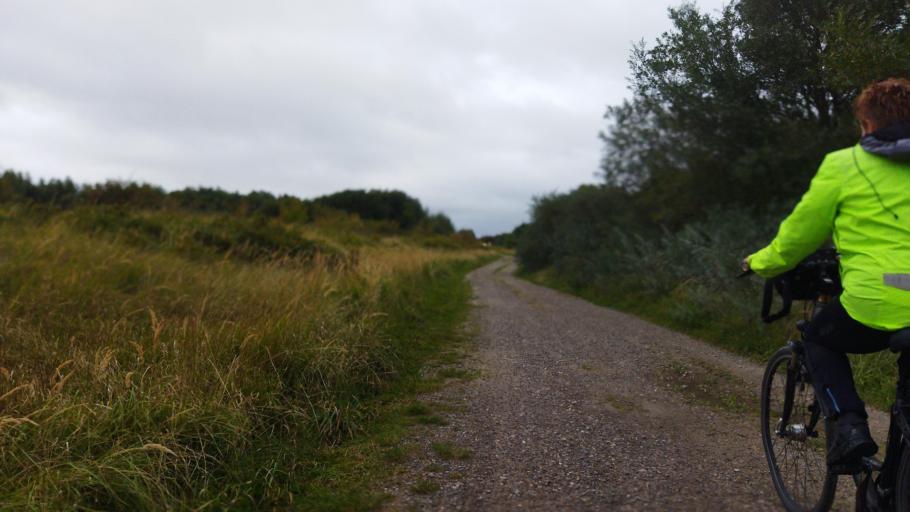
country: NL
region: Groningen
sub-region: Gemeente Delfzijl
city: Delfzijl
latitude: 53.3650
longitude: 7.0036
